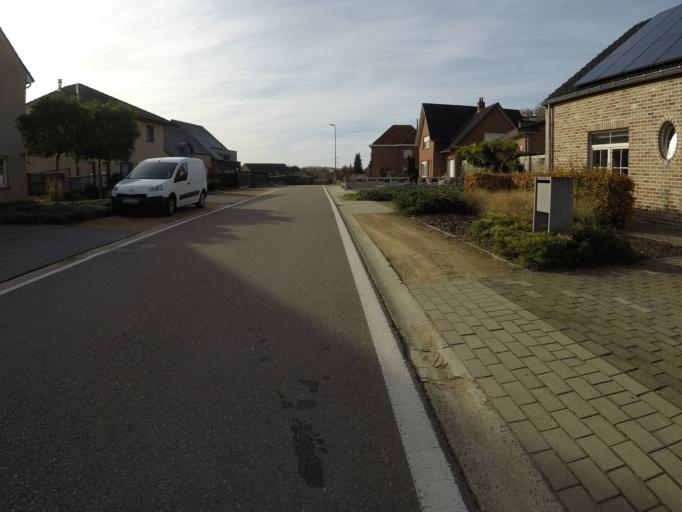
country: BE
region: Flanders
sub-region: Provincie Vlaams-Brabant
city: Begijnendijk
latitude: 50.9914
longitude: 4.7996
